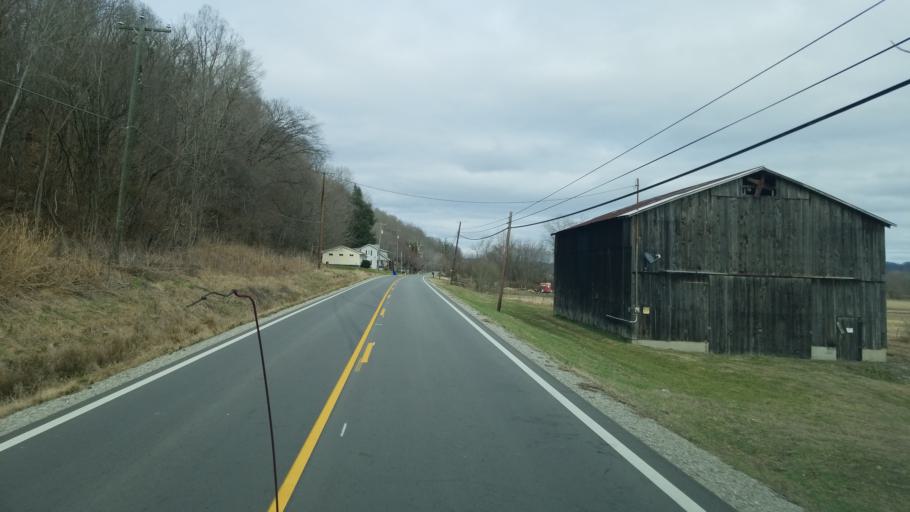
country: US
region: Ohio
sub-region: Scioto County
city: West Portsmouth
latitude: 38.6446
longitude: -83.1394
